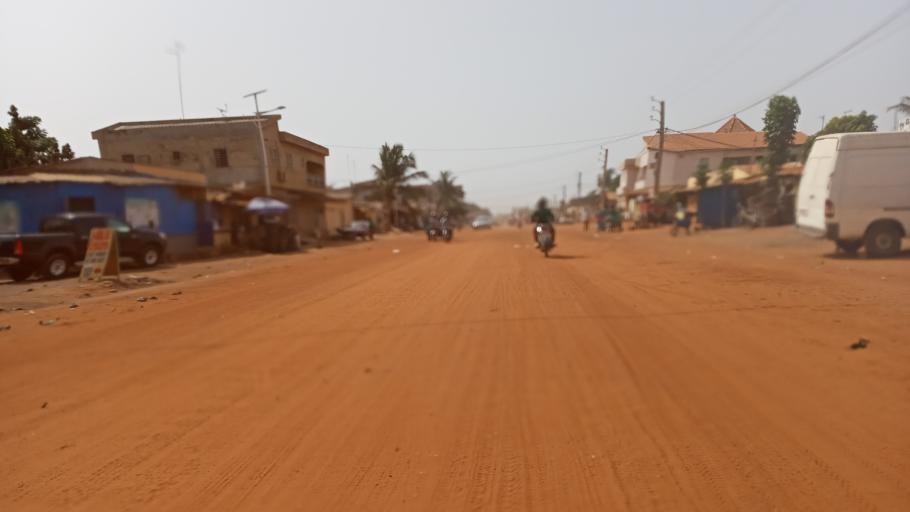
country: TG
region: Maritime
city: Lome
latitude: 6.2020
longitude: 1.1678
